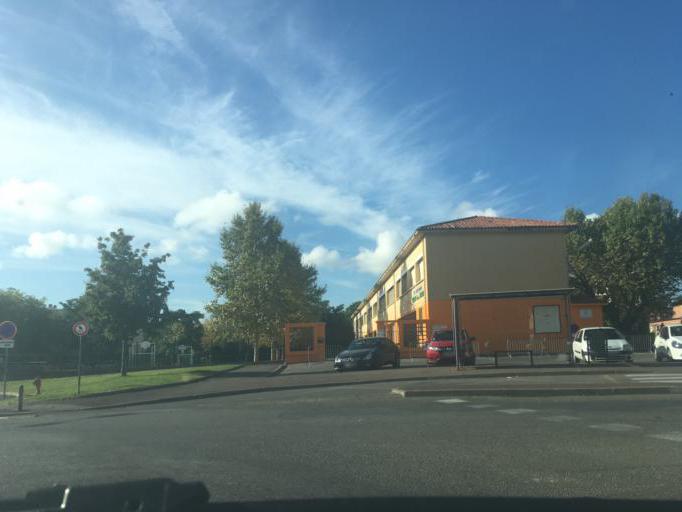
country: FR
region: Provence-Alpes-Cote d'Azur
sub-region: Departement du Var
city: Draguignan
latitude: 43.5409
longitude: 6.4571
